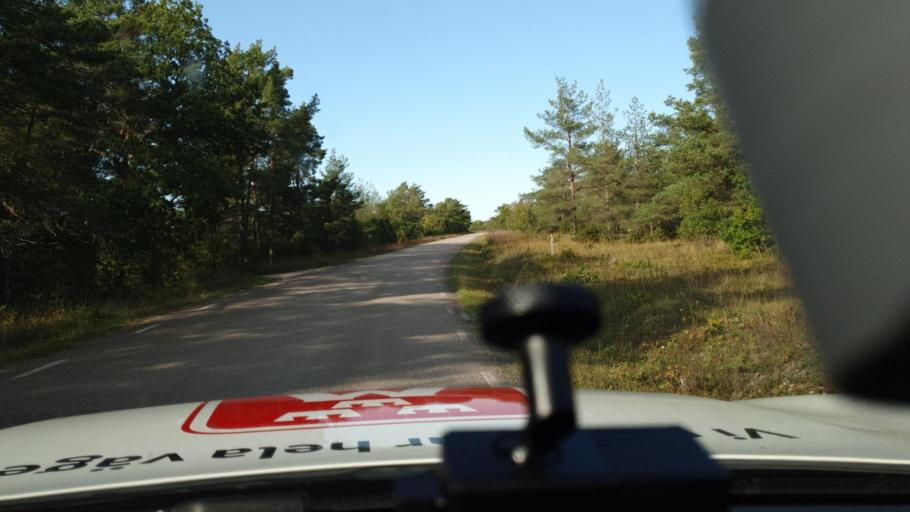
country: SE
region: Gotland
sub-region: Gotland
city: Slite
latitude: 57.6886
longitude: 18.6360
